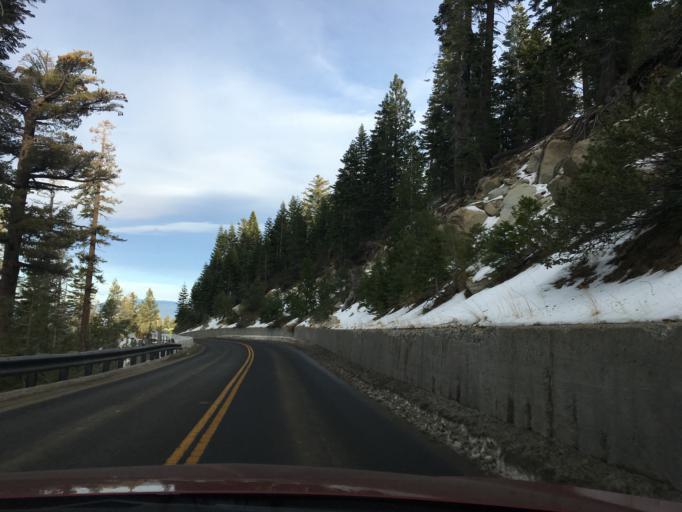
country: US
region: California
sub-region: El Dorado County
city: South Lake Tahoe
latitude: 38.9473
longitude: -120.0951
